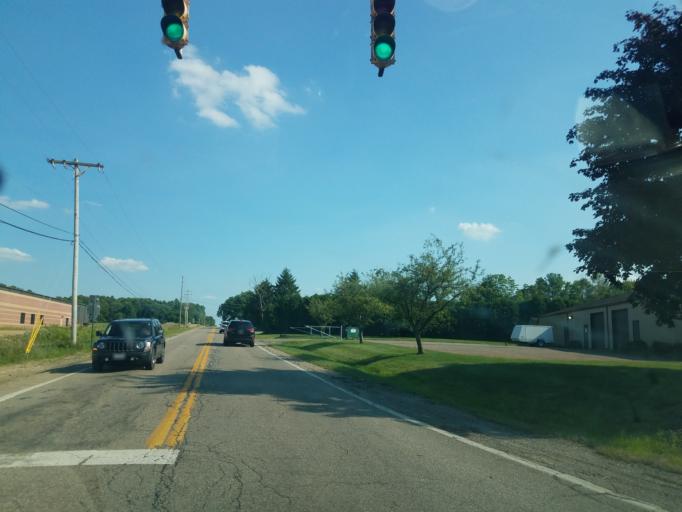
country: US
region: Ohio
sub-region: Stark County
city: Greentown
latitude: 40.9286
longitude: -81.4279
